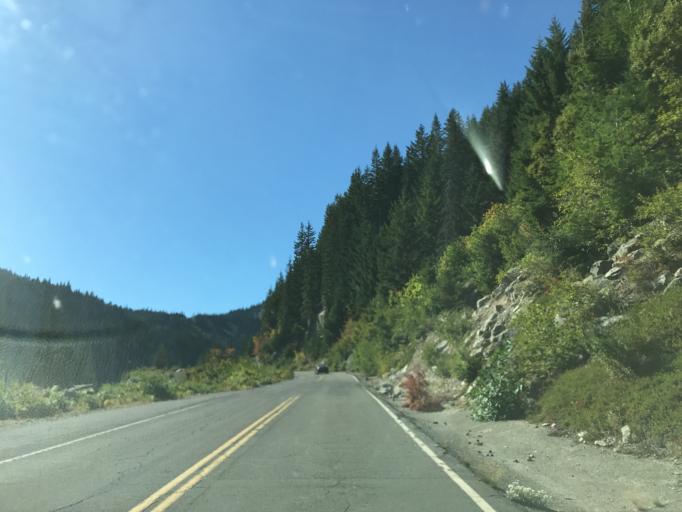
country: US
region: Washington
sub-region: Pierce County
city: Buckley
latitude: 46.7706
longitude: -121.6863
